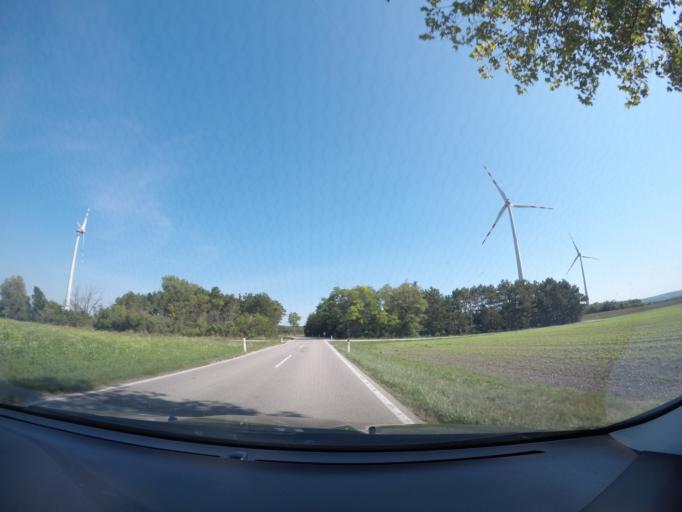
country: AT
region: Lower Austria
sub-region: Politischer Bezirk Baden
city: Seibersdorf
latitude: 47.9598
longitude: 16.4906
